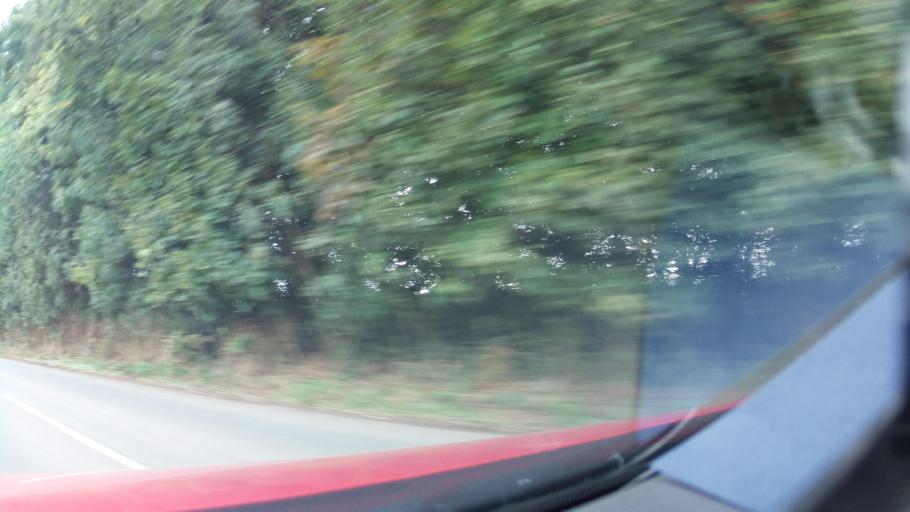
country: GB
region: England
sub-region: Staffordshire
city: Eccleshall
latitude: 52.9054
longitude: -2.2198
